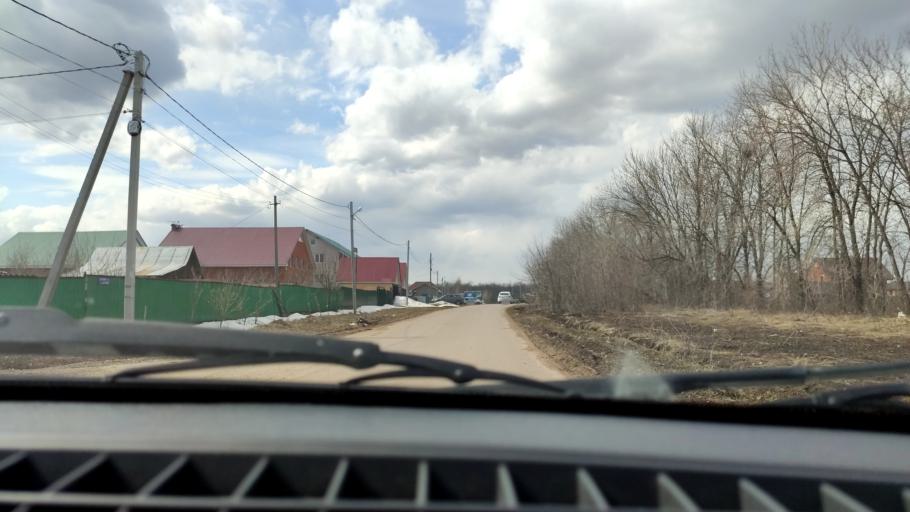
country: RU
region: Bashkortostan
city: Mikhaylovka
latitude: 54.8222
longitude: 55.8902
